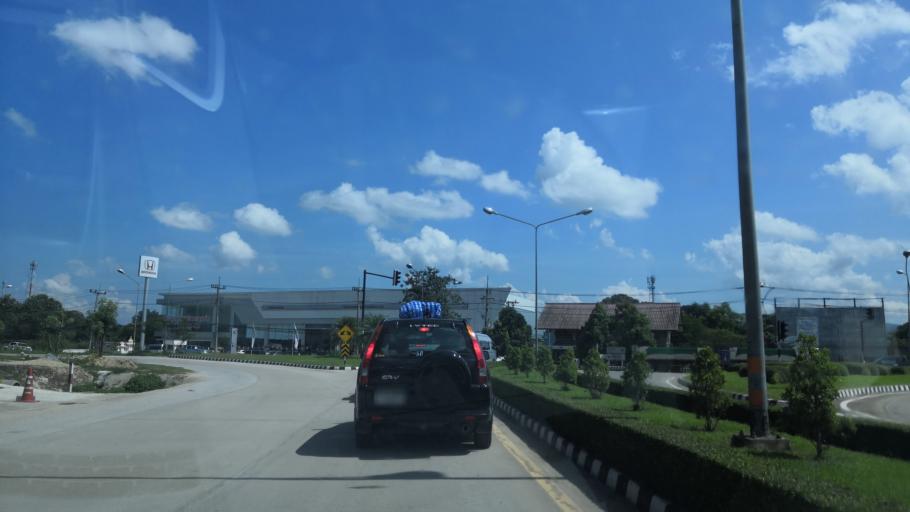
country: TH
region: Chiang Rai
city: Mae Lao
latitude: 19.8239
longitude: 99.7651
